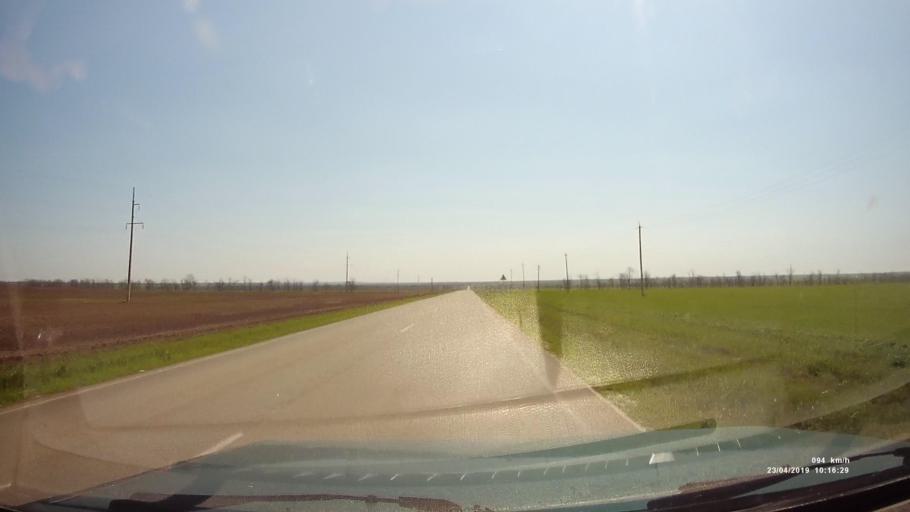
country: RU
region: Rostov
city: Sovetskoye
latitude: 46.6582
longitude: 42.3964
